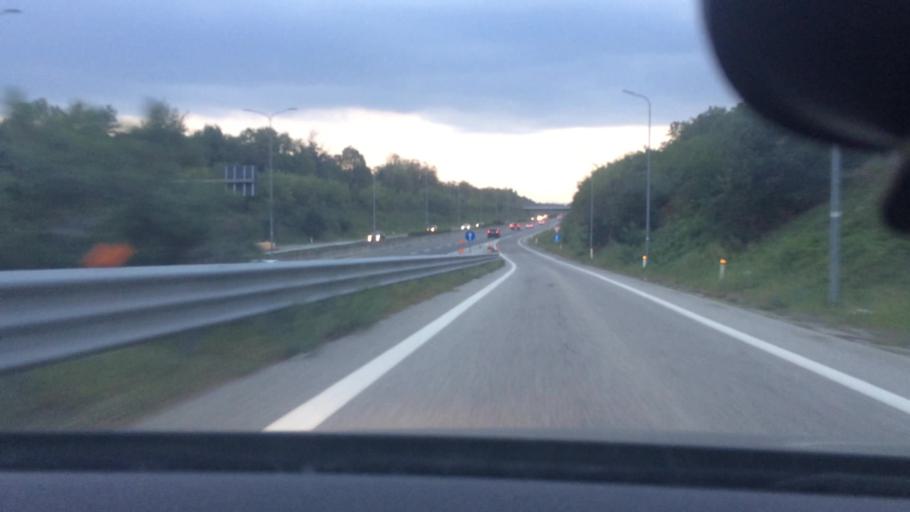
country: IT
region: Lombardy
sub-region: Provincia di Varese
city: Vizzola Ticino
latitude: 45.6093
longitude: 8.7100
